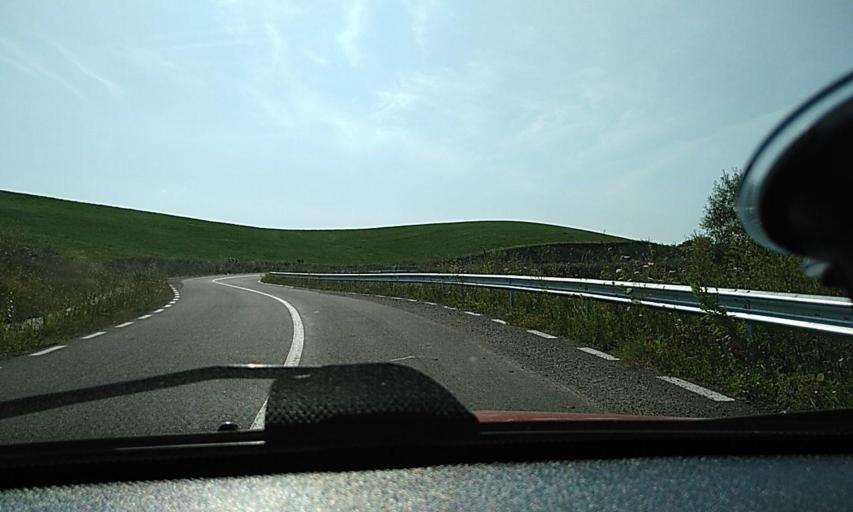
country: RO
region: Brasov
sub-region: Comuna Bunesti
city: Bunesti
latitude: 46.0677
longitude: 25.0782
